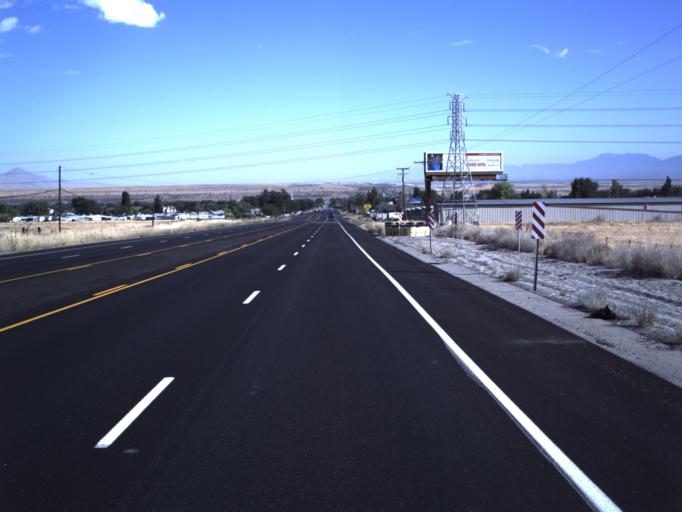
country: US
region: Utah
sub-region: Salt Lake County
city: Magna
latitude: 40.6851
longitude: -112.0918
